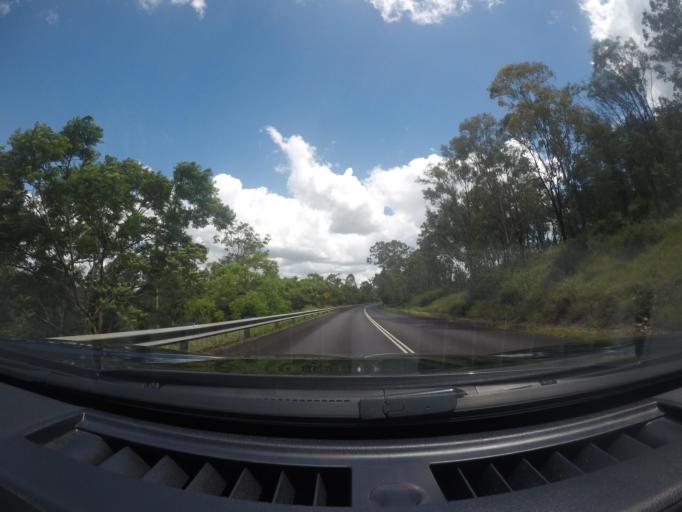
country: AU
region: Queensland
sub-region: Moreton Bay
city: Woodford
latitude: -27.1339
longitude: 152.5546
